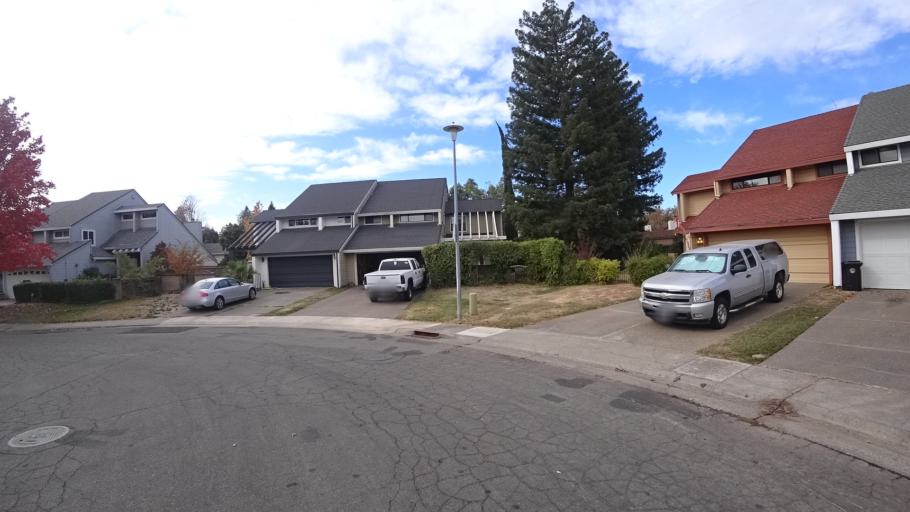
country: US
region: California
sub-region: Sacramento County
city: Fair Oaks
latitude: 38.6709
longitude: -121.2679
